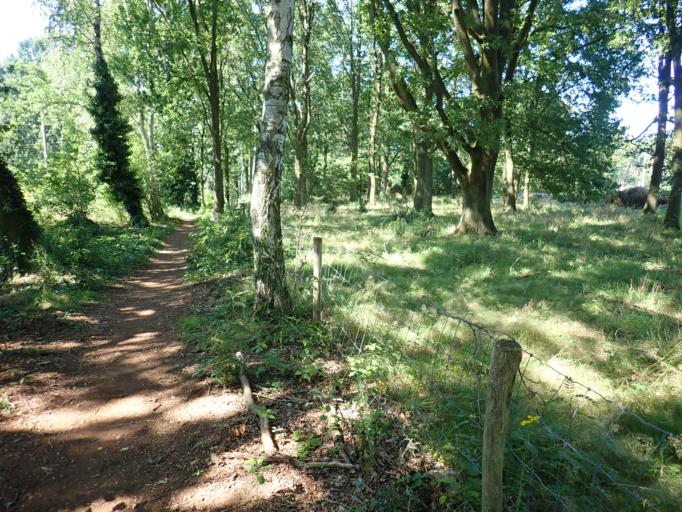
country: BE
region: Flanders
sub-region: Provincie Vlaams-Brabant
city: Scherpenheuvel-Zichem
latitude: 51.0273
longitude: 4.9546
